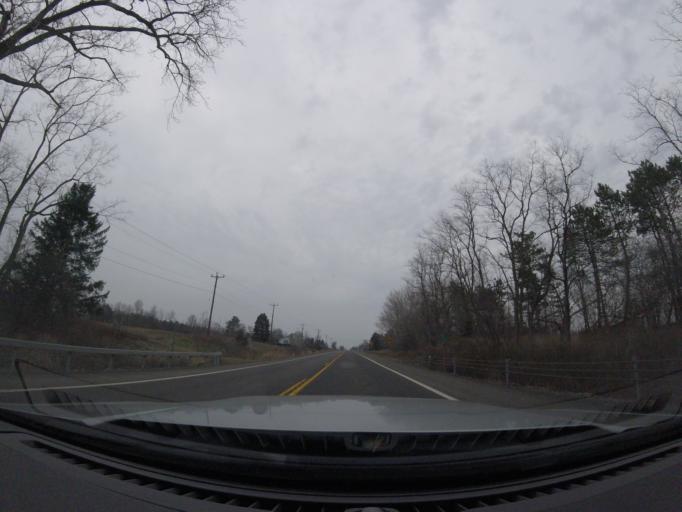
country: US
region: New York
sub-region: Yates County
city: Dundee
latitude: 42.6131
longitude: -76.9438
